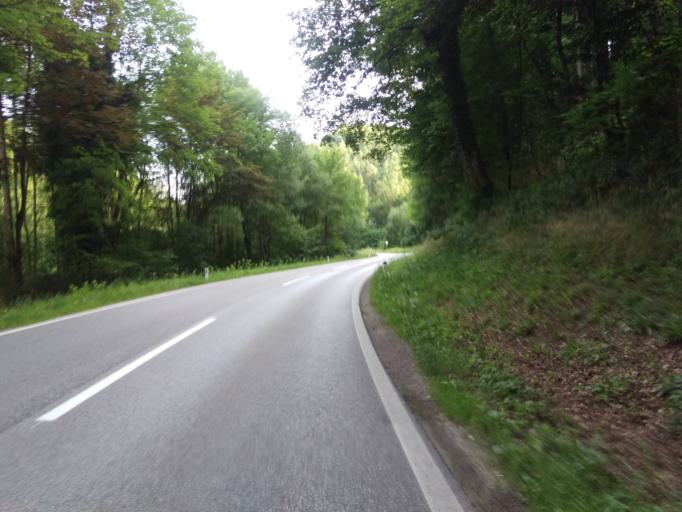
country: AT
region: Styria
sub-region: Politischer Bezirk Graz-Umgebung
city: Thal
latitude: 47.0763
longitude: 15.3645
